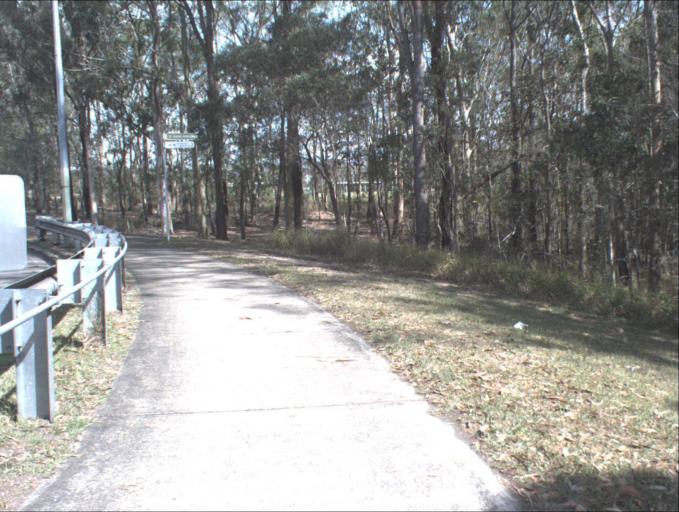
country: AU
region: Queensland
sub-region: Logan
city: Slacks Creek
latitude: -27.6533
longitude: 153.1408
